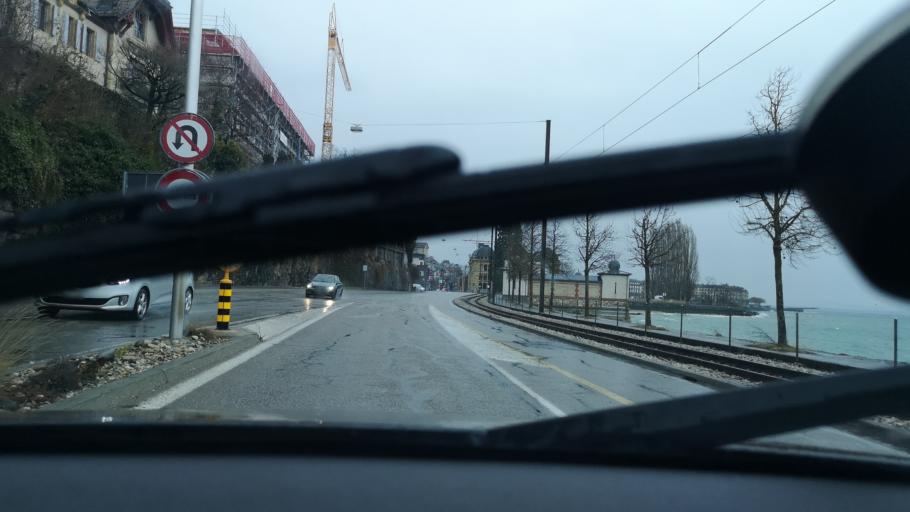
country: CH
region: Neuchatel
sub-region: Neuchatel District
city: Neuchatel
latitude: 46.9879
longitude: 6.9190
